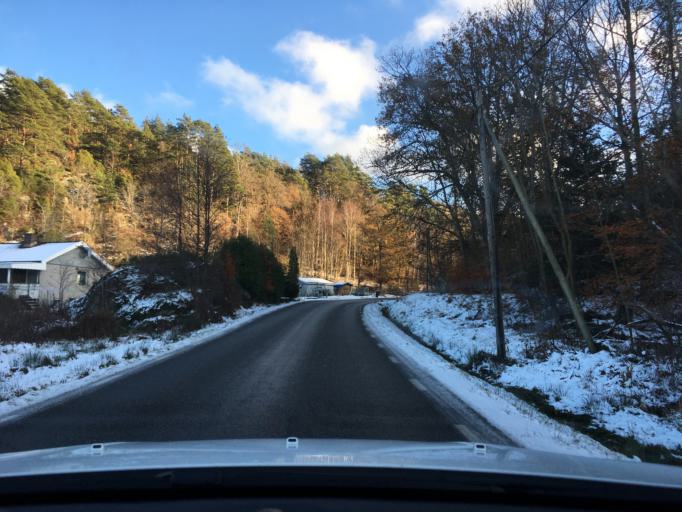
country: SE
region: Vaestra Goetaland
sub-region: Tjorns Kommun
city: Myggenas
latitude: 58.0588
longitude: 11.6907
